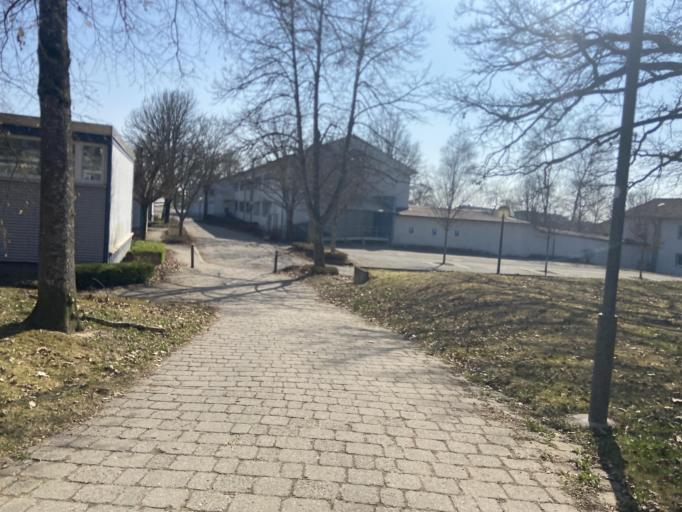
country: DE
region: Baden-Wuerttemberg
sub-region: Tuebingen Region
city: Sigmaringen
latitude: 48.0888
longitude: 9.2402
